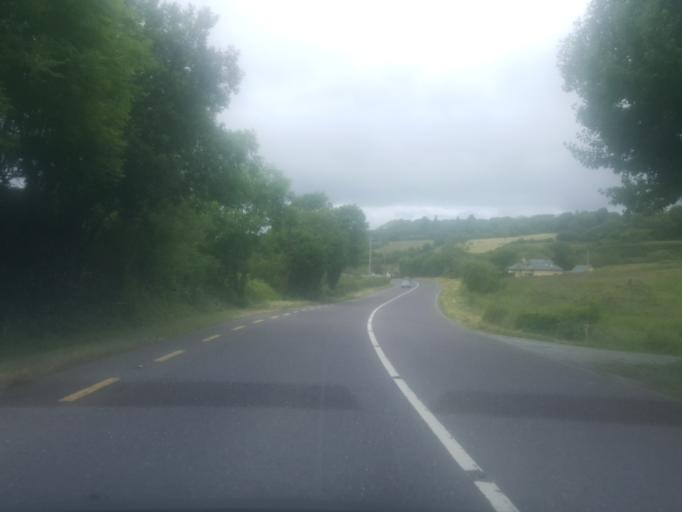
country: IE
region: Munster
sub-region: Ciarrai
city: Cill Airne
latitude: 52.1288
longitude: -9.5392
